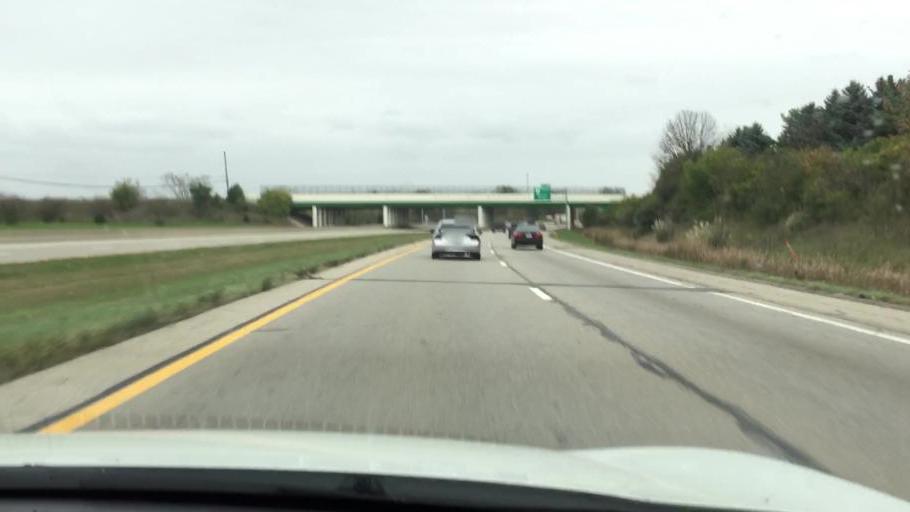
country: US
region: Ohio
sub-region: Union County
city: Marysville
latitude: 40.2539
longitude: -83.3695
